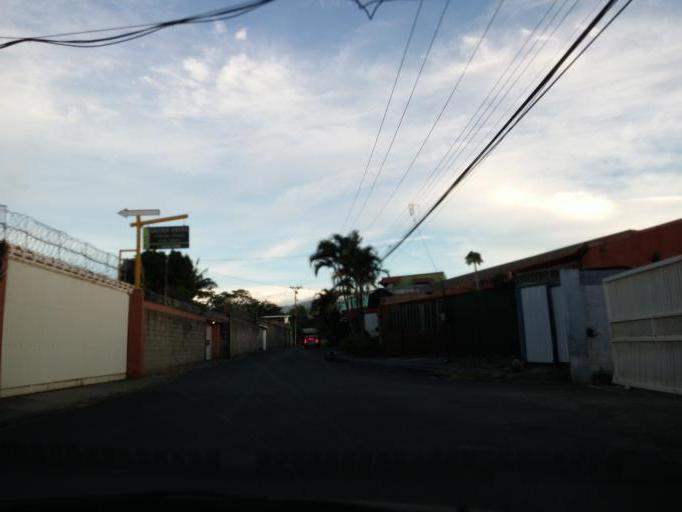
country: CR
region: Alajuela
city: Alajuela
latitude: 10.0008
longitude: -84.2249
